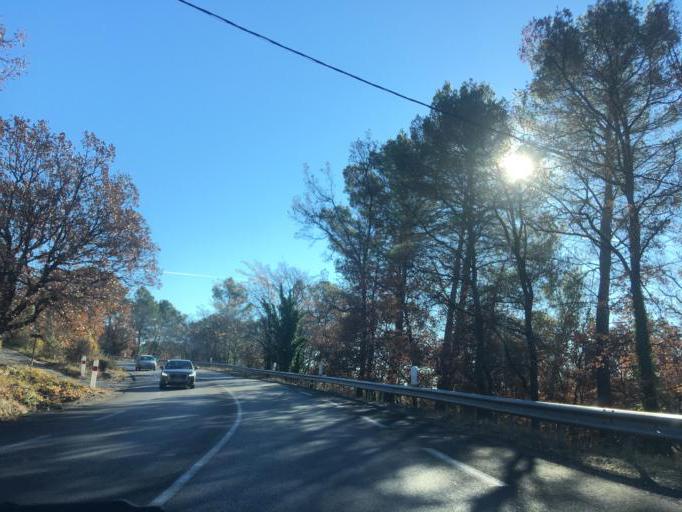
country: FR
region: Provence-Alpes-Cote d'Azur
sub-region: Departement du Var
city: Flayosc
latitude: 43.5422
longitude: 6.3617
